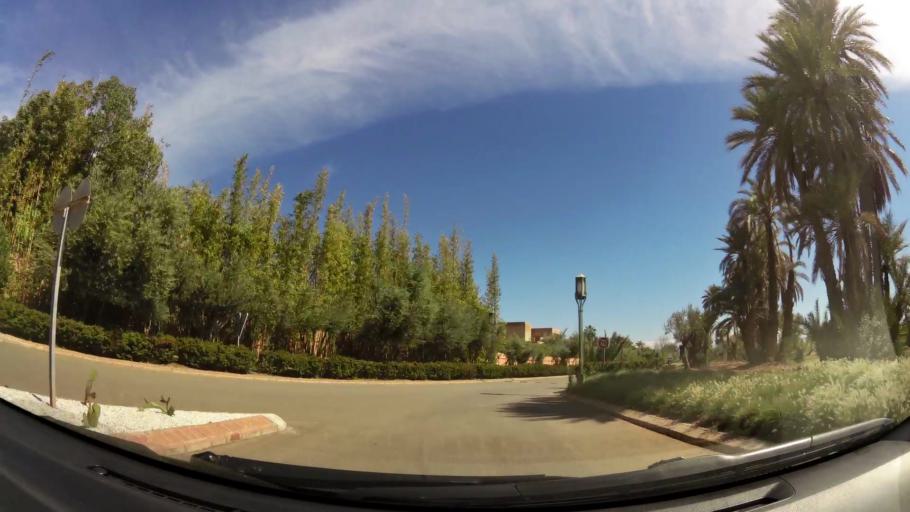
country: MA
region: Marrakech-Tensift-Al Haouz
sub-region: Marrakech
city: Marrakesh
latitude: 31.6187
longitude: -7.9369
